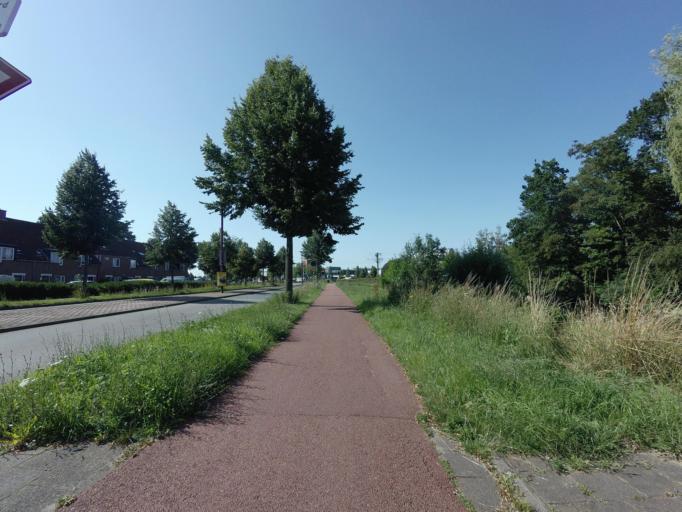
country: NL
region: Utrecht
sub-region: Gemeente Nieuwegein
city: Nieuwegein
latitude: 52.0448
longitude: 5.0922
